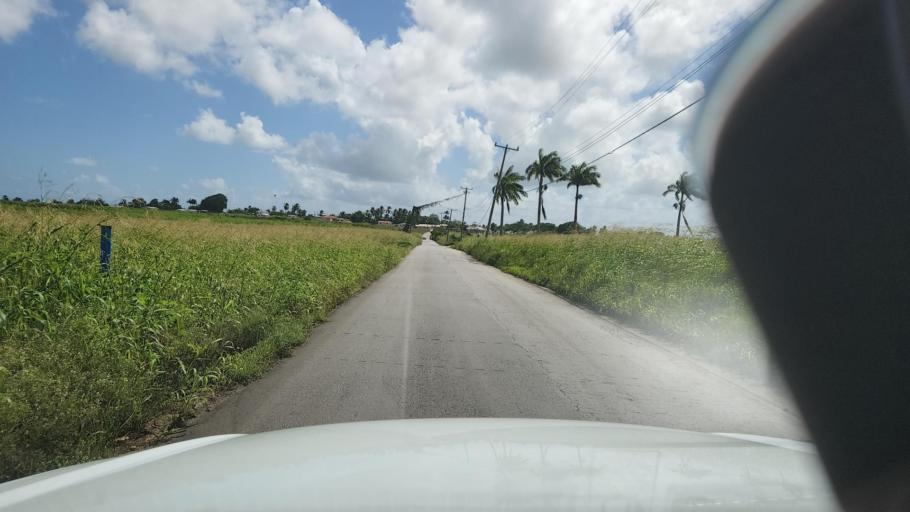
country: BB
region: Saint John
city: Four Cross Roads
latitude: 13.1683
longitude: -59.4851
